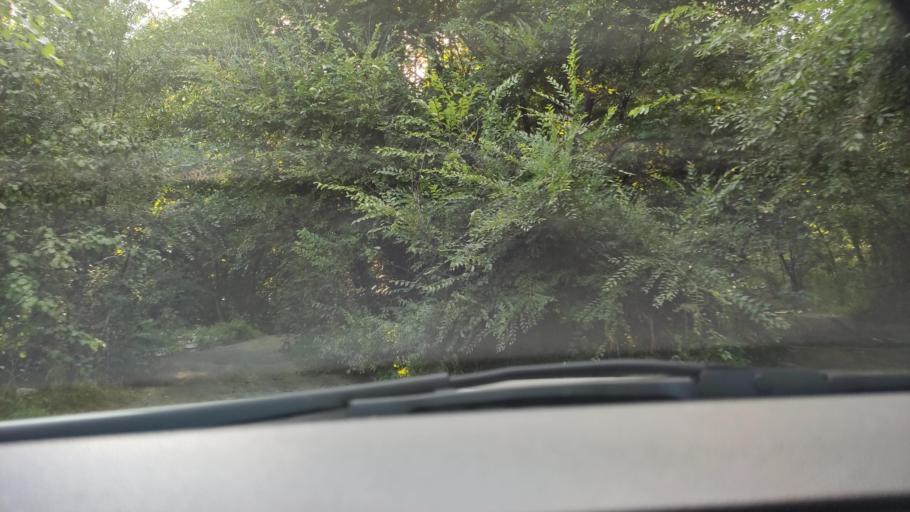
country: RU
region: Voronezj
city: Pridonskoy
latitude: 51.6832
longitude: 39.0514
